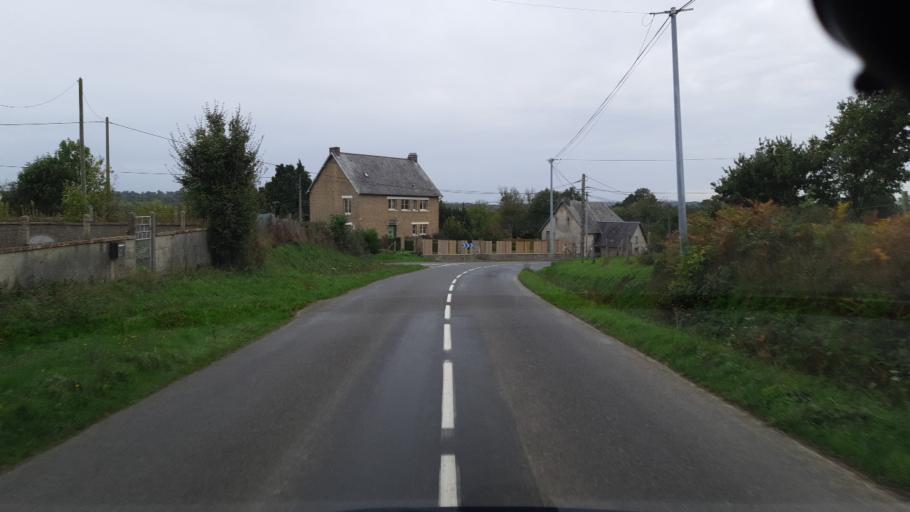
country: FR
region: Lower Normandy
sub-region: Departement de la Manche
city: Hambye
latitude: 48.9616
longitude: -1.2623
